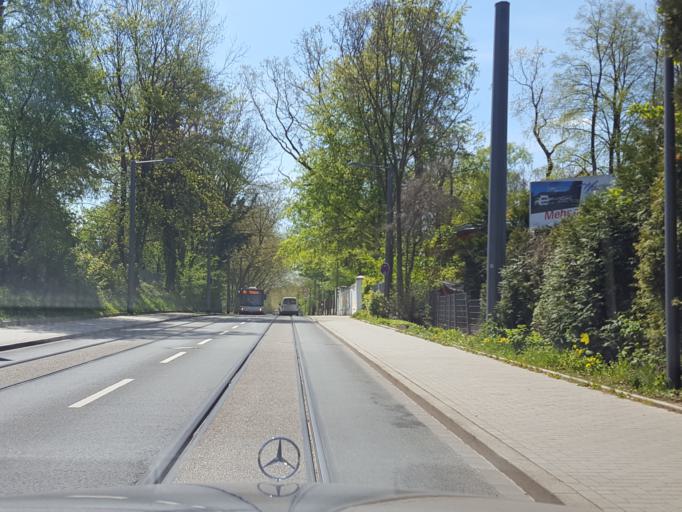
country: DE
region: North Rhine-Westphalia
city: Witten
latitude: 51.4697
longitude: 7.3233
